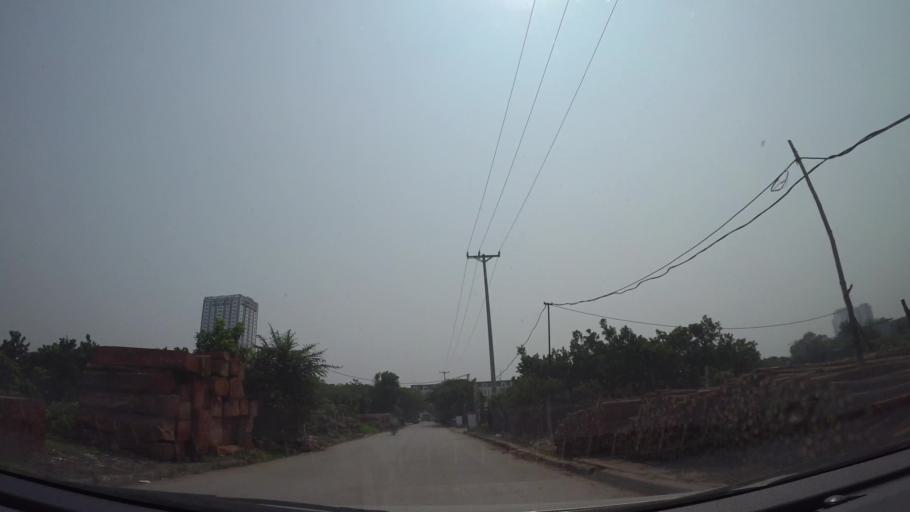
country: VN
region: Ha Noi
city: Ha Dong
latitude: 20.9893
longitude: 105.7677
